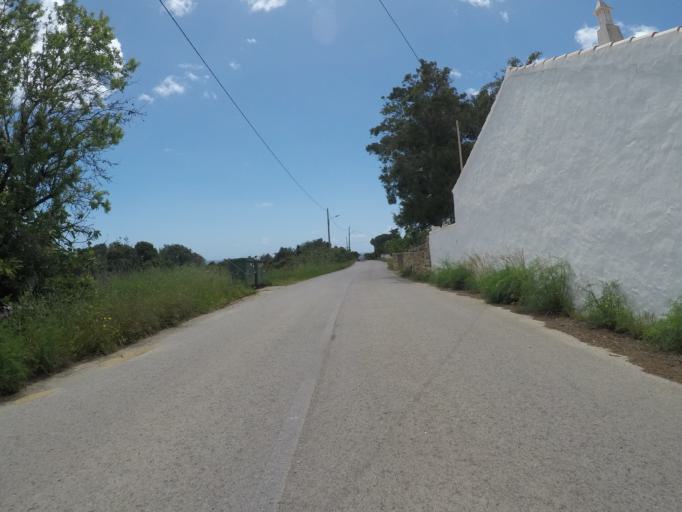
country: PT
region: Faro
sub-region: Lagoa
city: Carvoeiro
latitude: 37.0938
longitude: -8.4194
